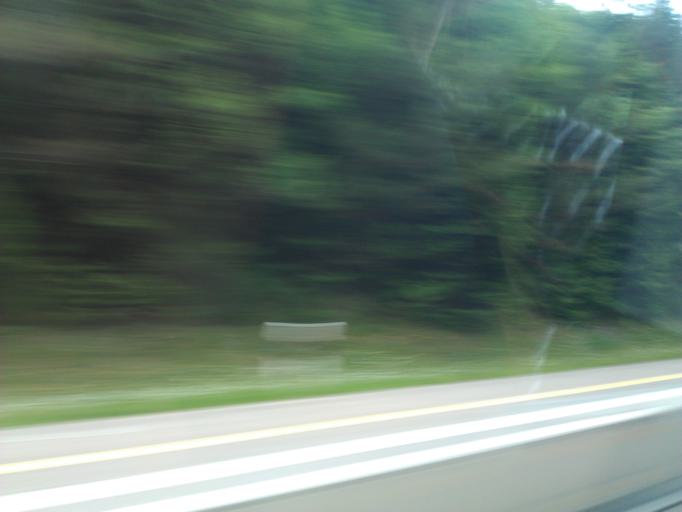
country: DE
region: Rheinland-Pfalz
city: Hinzert-Polert
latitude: 49.7182
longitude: 6.8928
